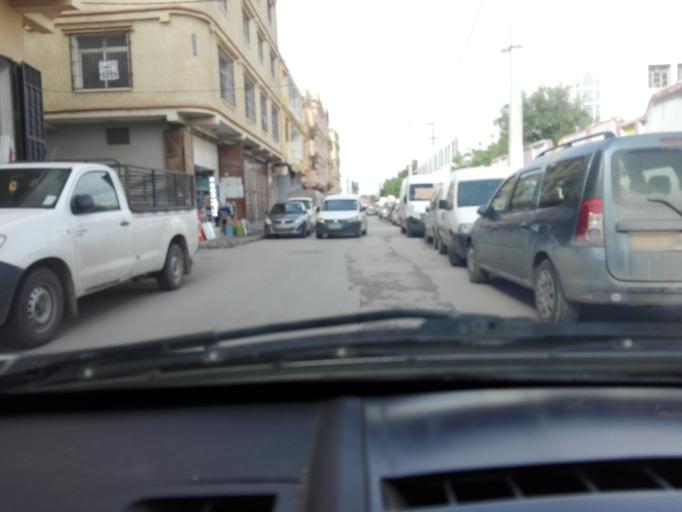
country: DZ
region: Alger
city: Dar el Beida
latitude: 36.7328
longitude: 3.2328
